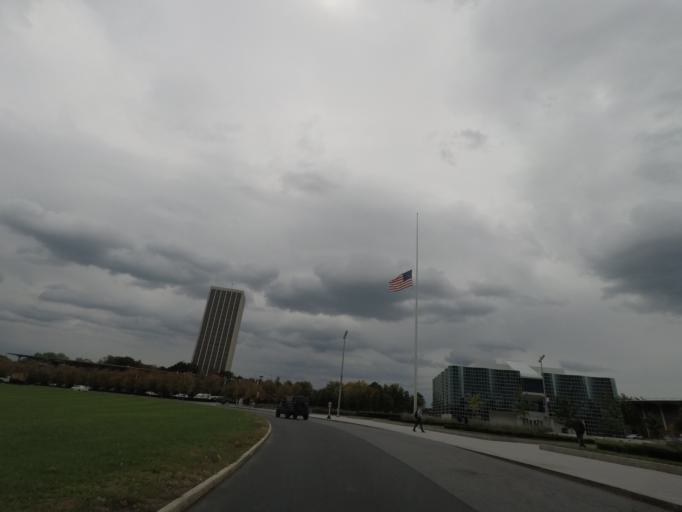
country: US
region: New York
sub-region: Albany County
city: Roessleville
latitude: 42.6877
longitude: -73.8226
